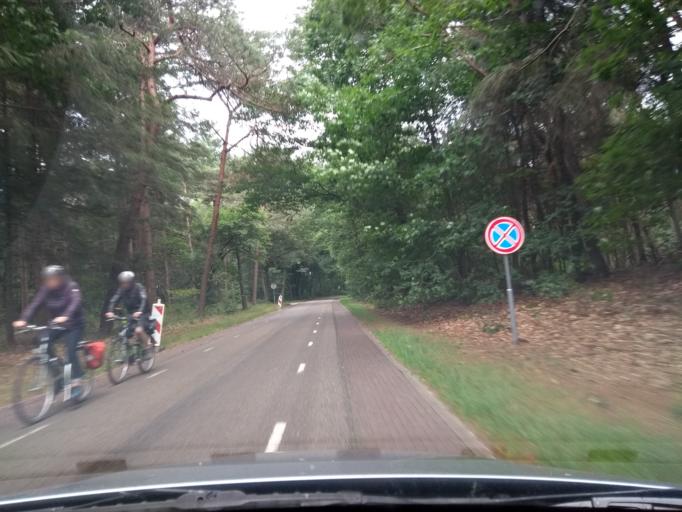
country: NL
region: Overijssel
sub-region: Gemeente Twenterand
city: Den Ham
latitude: 52.4575
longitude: 6.4026
